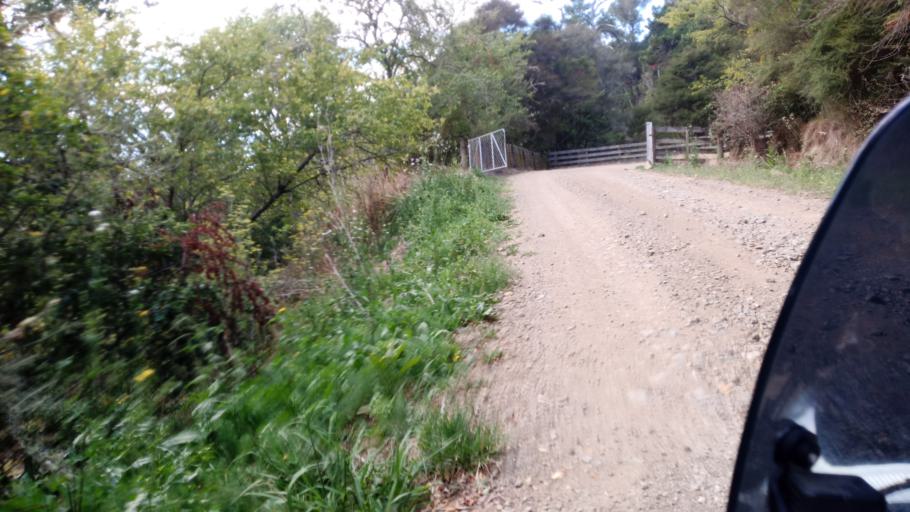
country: NZ
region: Gisborne
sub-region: Gisborne District
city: Gisborne
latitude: -38.4705
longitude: 177.6657
